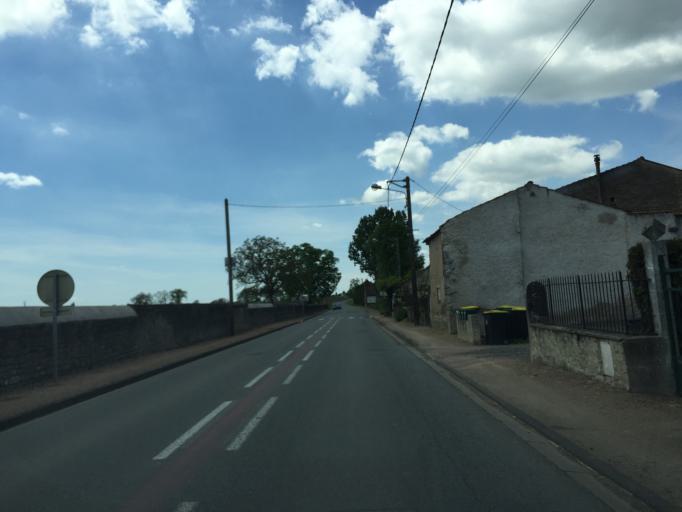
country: FR
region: Auvergne
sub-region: Departement du Puy-de-Dome
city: Aigueperse
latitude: 46.0371
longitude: 3.2522
